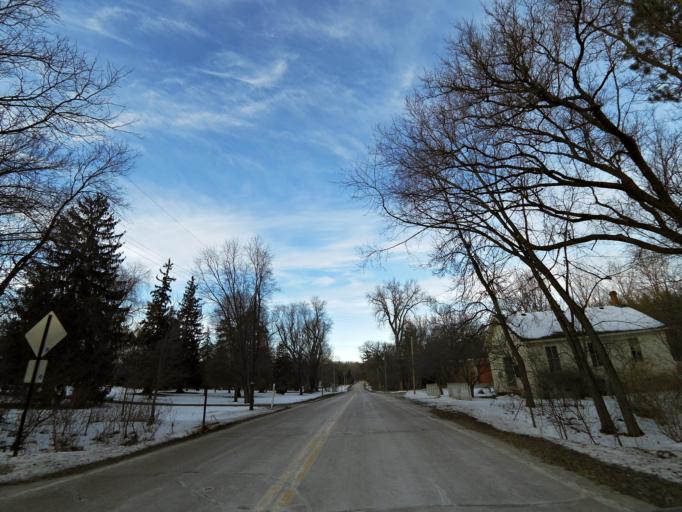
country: US
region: Minnesota
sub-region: Washington County
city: Afton
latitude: 44.9239
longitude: -92.8020
